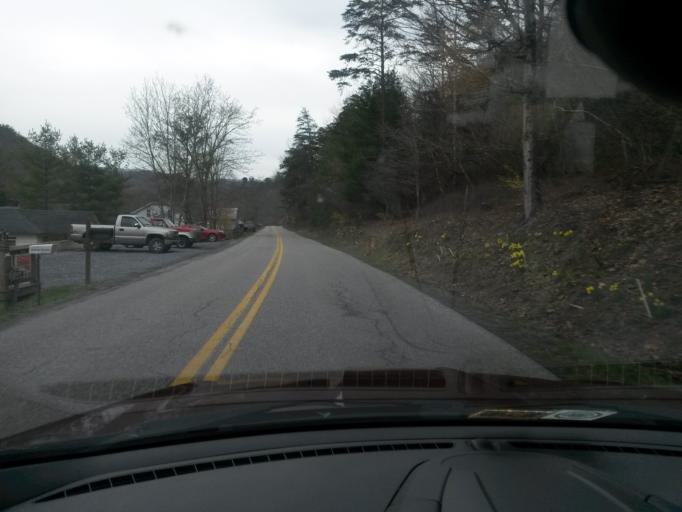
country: US
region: Virginia
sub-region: Bath County
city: Warm Springs
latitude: 38.0091
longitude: -79.8760
